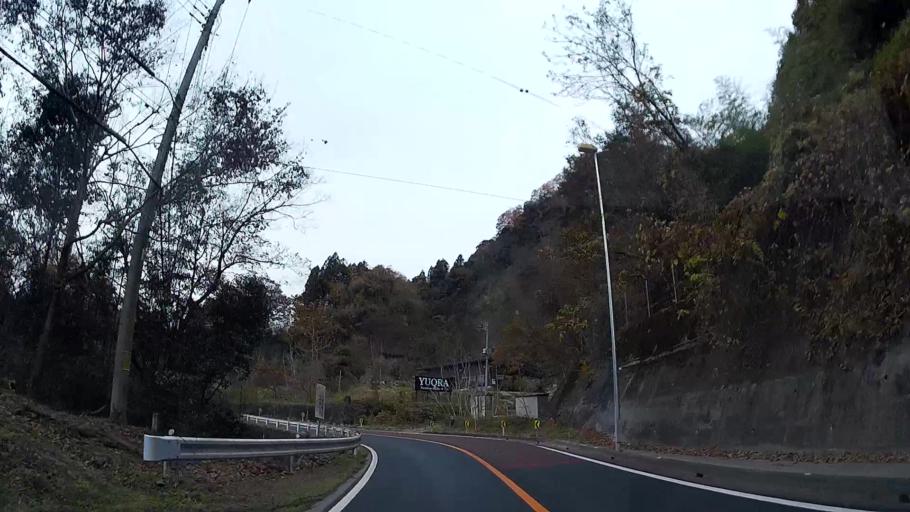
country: JP
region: Saitama
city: Chichibu
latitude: 35.9623
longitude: 138.9980
